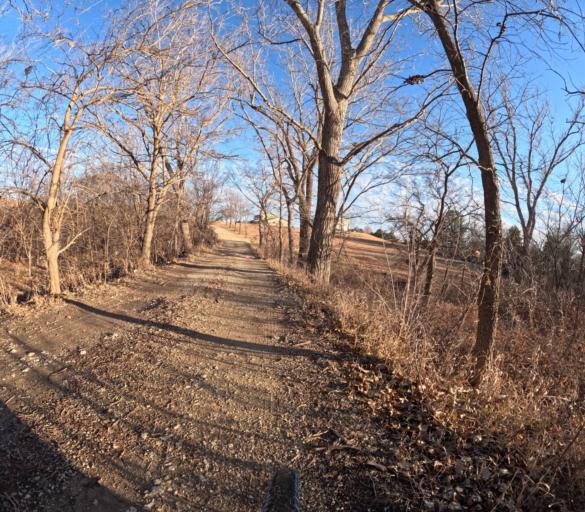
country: US
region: Kansas
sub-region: Riley County
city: Ogden
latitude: 39.2195
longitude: -96.6858
